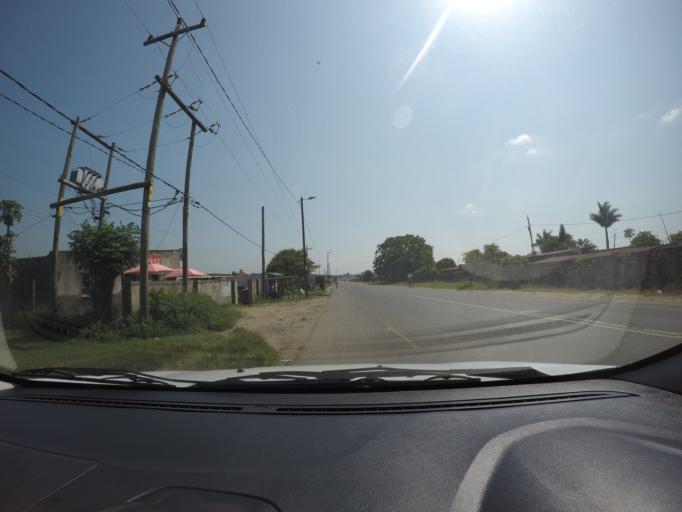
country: ZA
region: KwaZulu-Natal
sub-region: uThungulu District Municipality
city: eSikhawini
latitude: -28.8755
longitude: 31.8955
